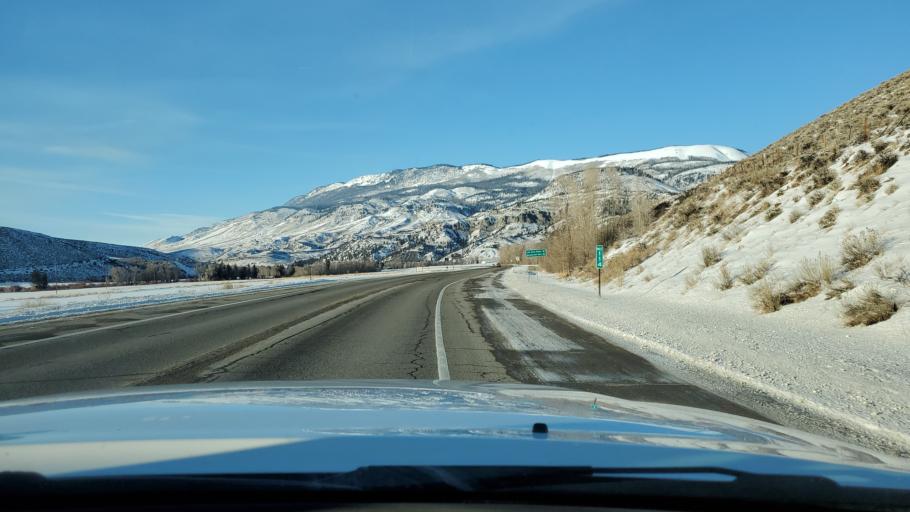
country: US
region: Colorado
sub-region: Summit County
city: Silverthorne
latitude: 39.7829
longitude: -106.1564
